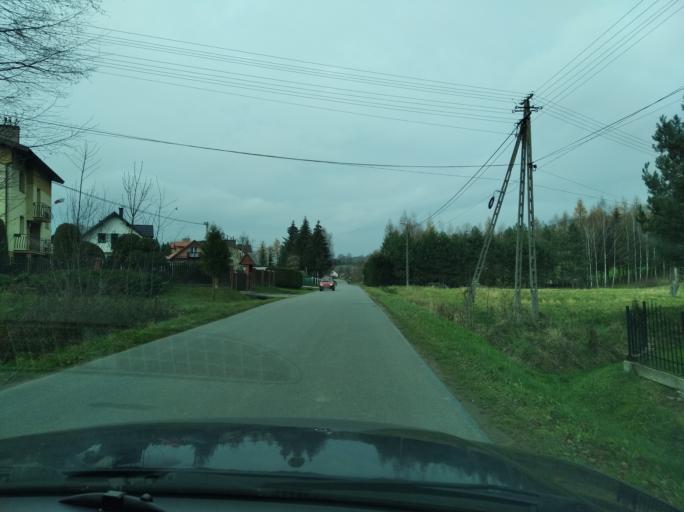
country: PL
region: Subcarpathian Voivodeship
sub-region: Powiat krosnienski
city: Odrzykon
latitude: 49.7732
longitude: 21.7818
